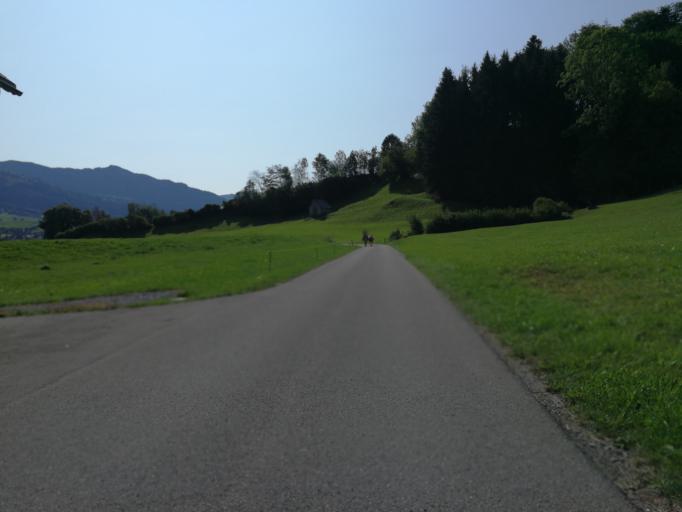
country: CH
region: Saint Gallen
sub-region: Wahlkreis Toggenburg
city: Krummenau
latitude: 47.2381
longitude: 9.1770
